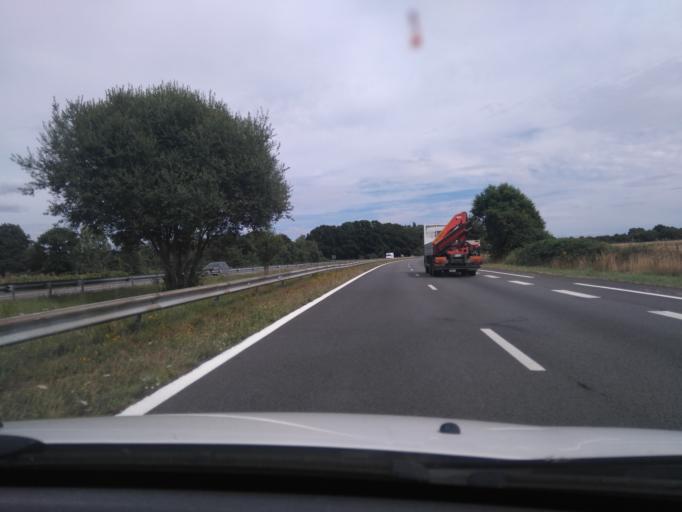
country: FR
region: Brittany
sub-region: Departement d'Ille-et-Vilaine
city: Montauban-de-Bretagne
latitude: 48.2066
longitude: -2.0411
